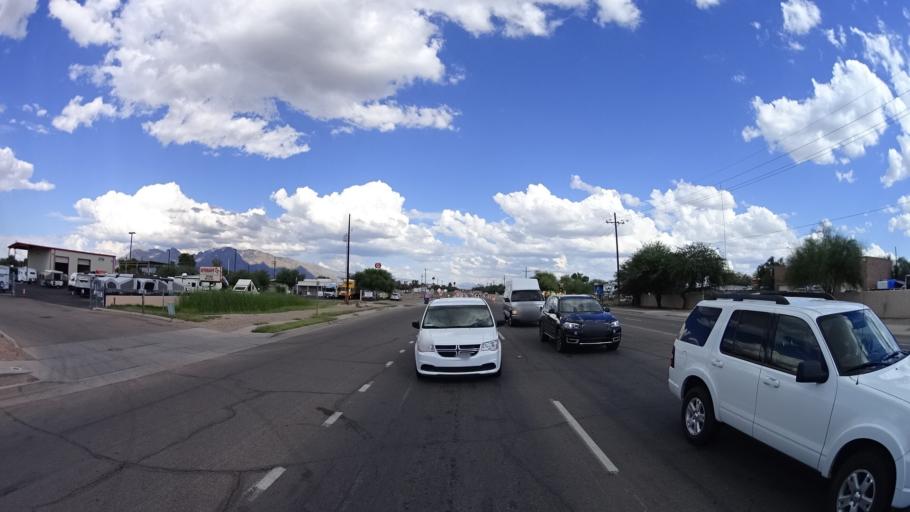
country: US
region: Arizona
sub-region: Pima County
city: Flowing Wells
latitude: 32.2941
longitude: -111.0263
